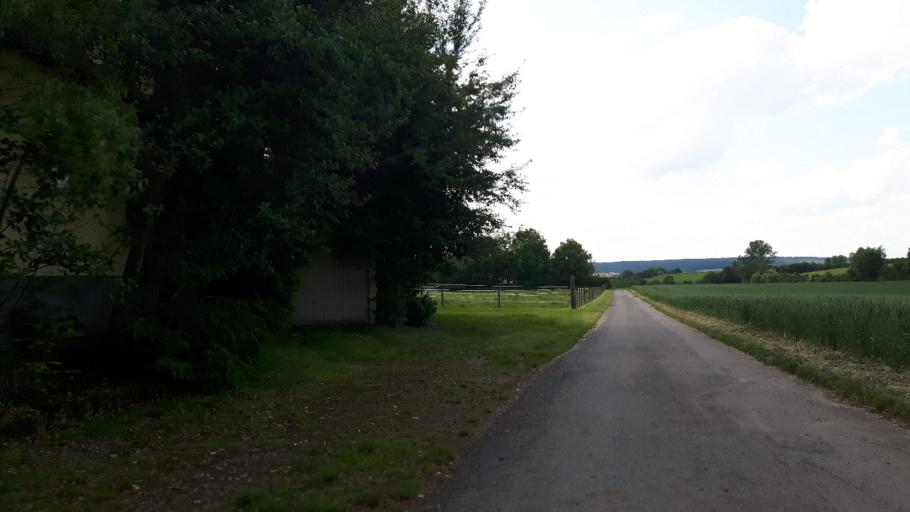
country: DE
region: Bavaria
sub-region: Regierungsbezirk Unterfranken
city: Reichenberg
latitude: 49.7120
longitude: 9.9271
